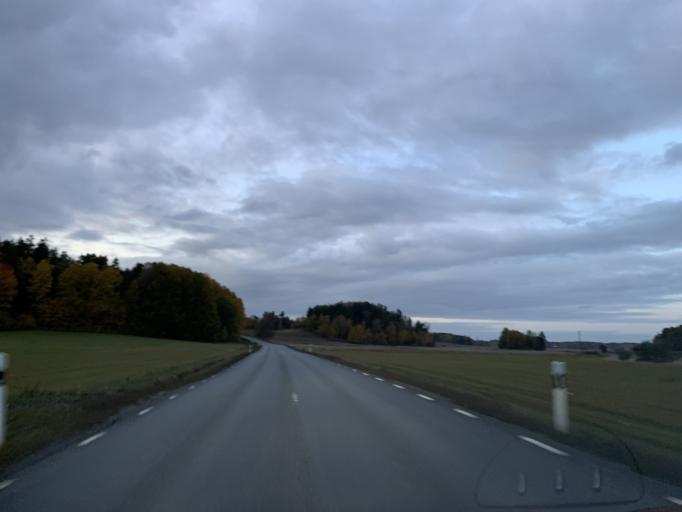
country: SE
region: Stockholm
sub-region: Nynashamns Kommun
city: Osmo
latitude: 59.0142
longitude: 17.8053
